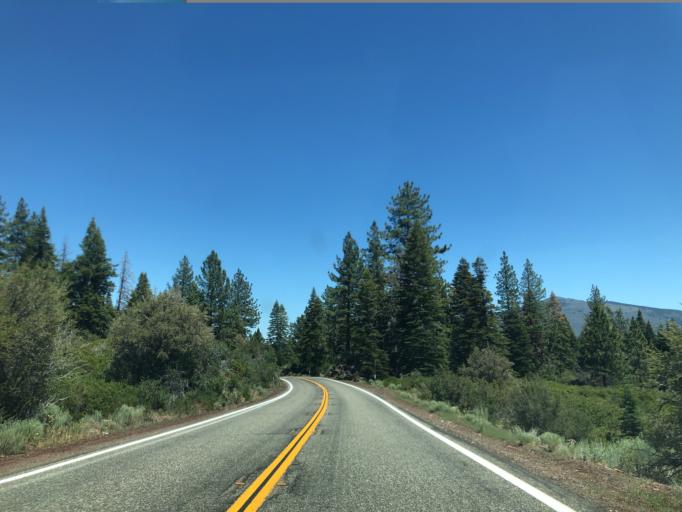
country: US
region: California
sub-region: Shasta County
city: Burney
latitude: 40.6177
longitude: -121.4945
